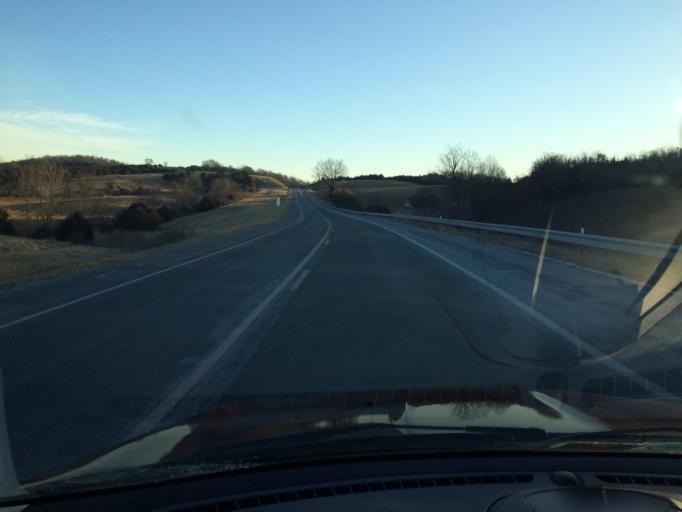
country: US
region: Virginia
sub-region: City of Staunton
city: Staunton
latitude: 38.1865
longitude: -79.0556
